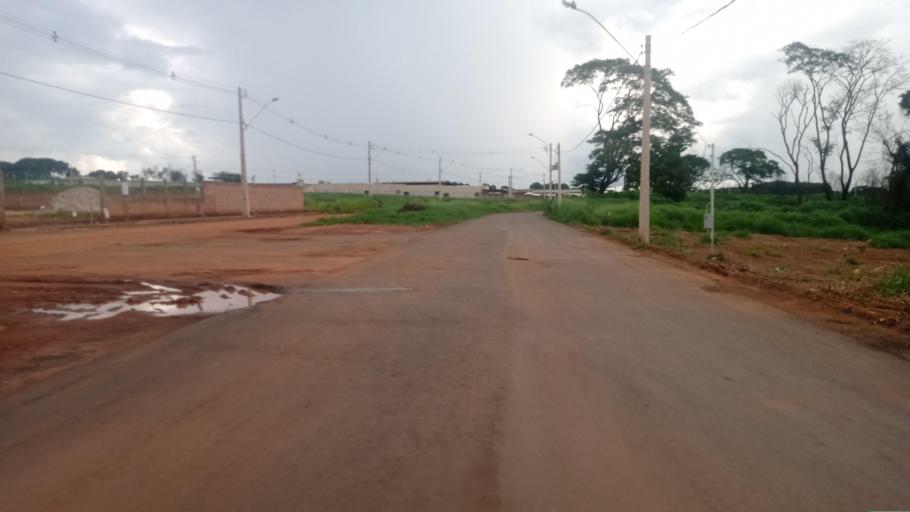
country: BR
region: Goias
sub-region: Senador Canedo
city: Senador Canedo
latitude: -16.7154
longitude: -49.1194
